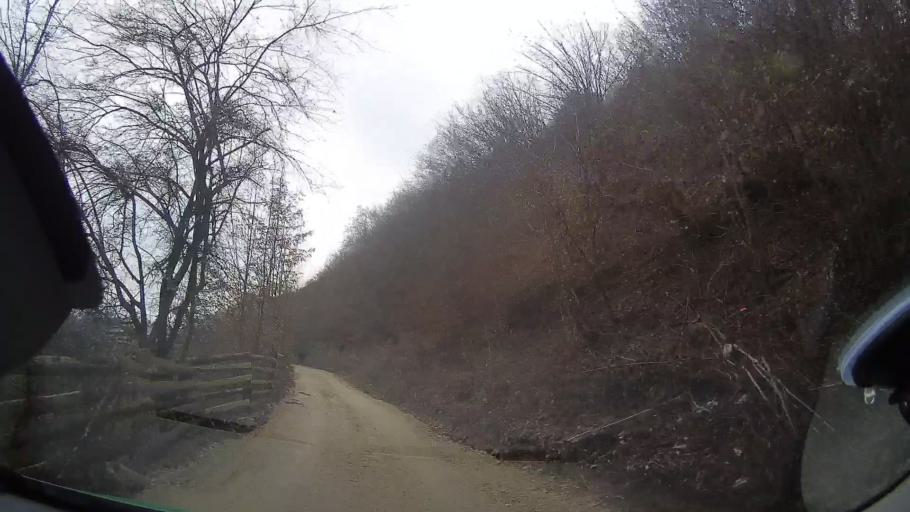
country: RO
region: Cluj
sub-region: Comuna Maguri-Racatau
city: Maguri-Racatau
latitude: 46.6538
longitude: 23.2023
